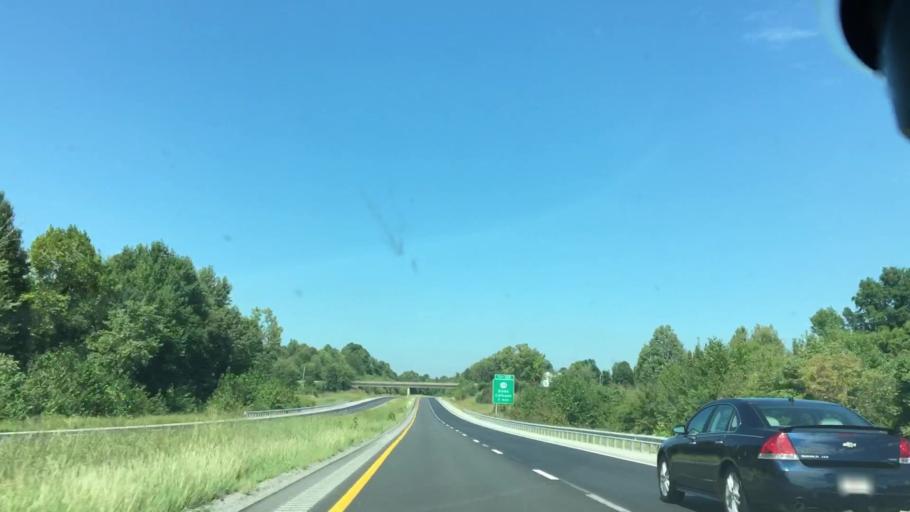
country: US
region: Kentucky
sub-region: Hopkins County
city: Madisonville
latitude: 37.4555
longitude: -87.4788
